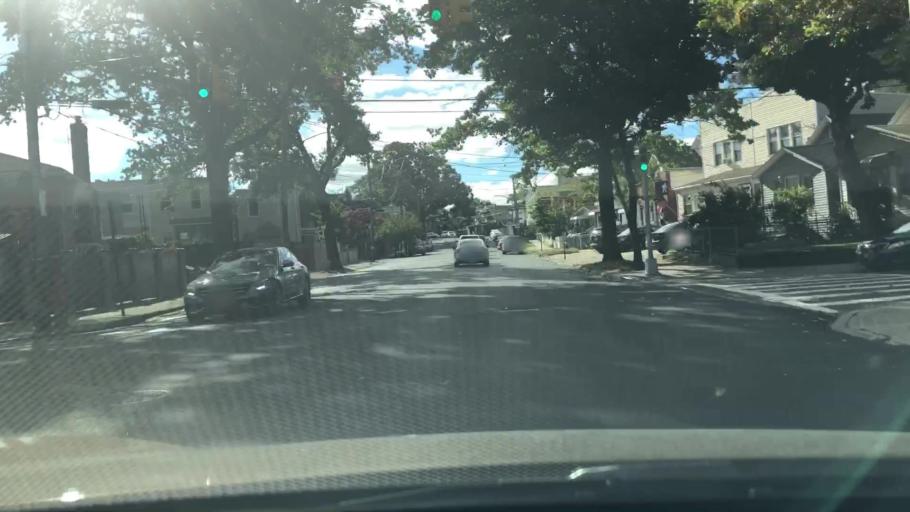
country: US
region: New York
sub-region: Queens County
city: Long Island City
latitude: 40.7247
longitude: -73.8946
